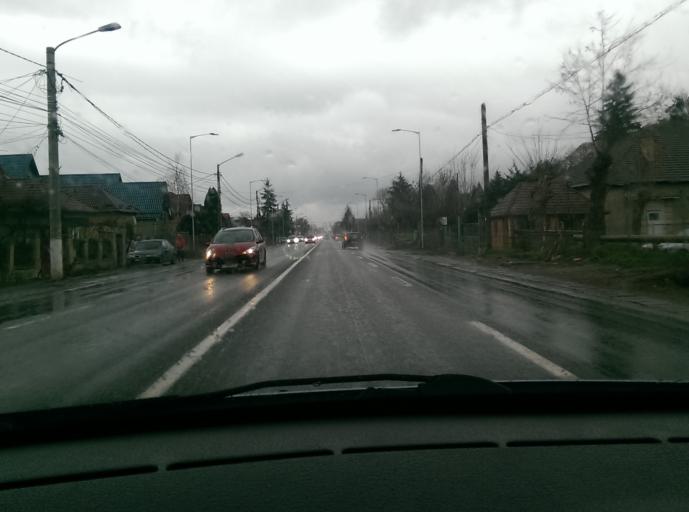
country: RO
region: Cluj
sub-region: Comuna Floresti
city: Floresti
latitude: 46.7483
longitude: 23.5078
